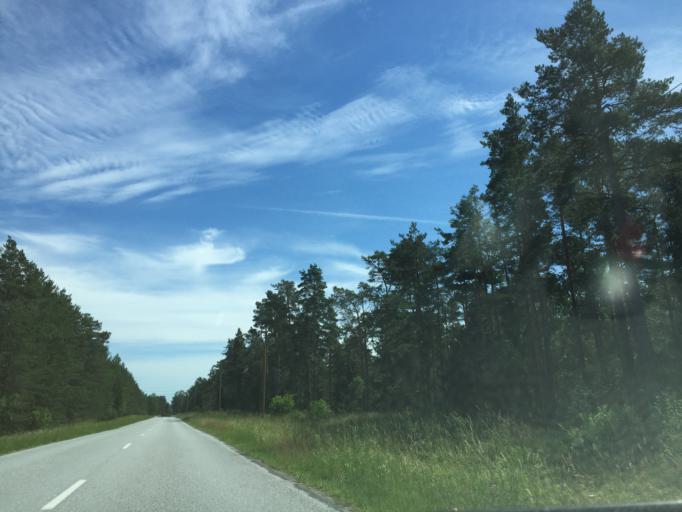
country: LV
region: Rojas
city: Roja
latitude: 57.5808
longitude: 22.6225
